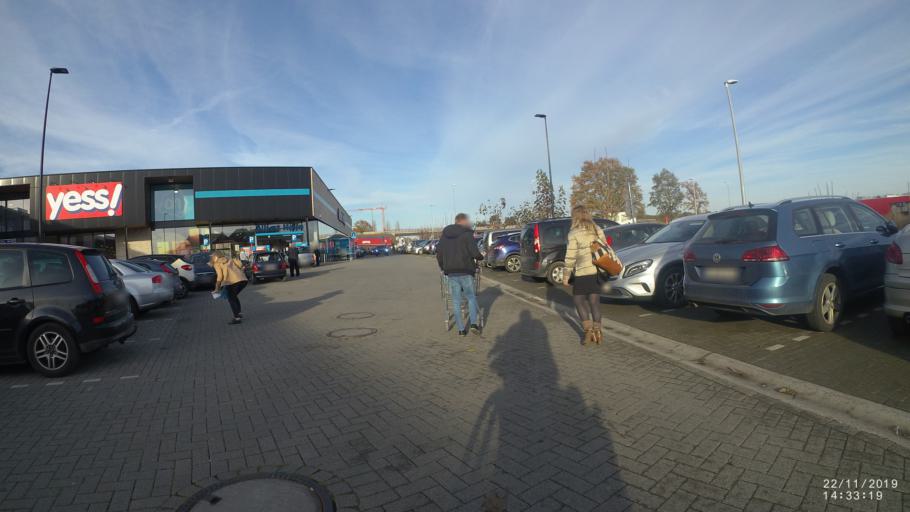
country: BE
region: Flanders
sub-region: Provincie Vlaams-Brabant
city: Aarschot
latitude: 50.9995
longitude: 4.8343
